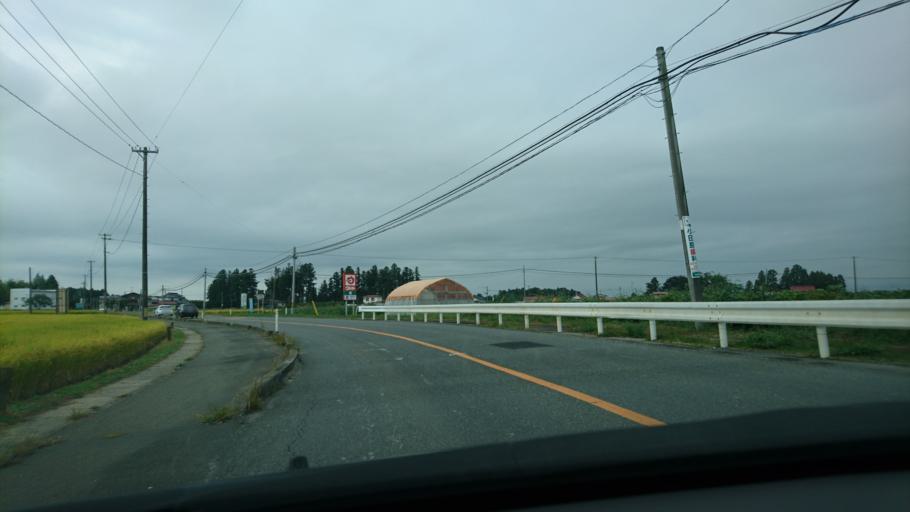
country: JP
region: Iwate
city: Ichinoseki
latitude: 38.7710
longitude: 141.0956
